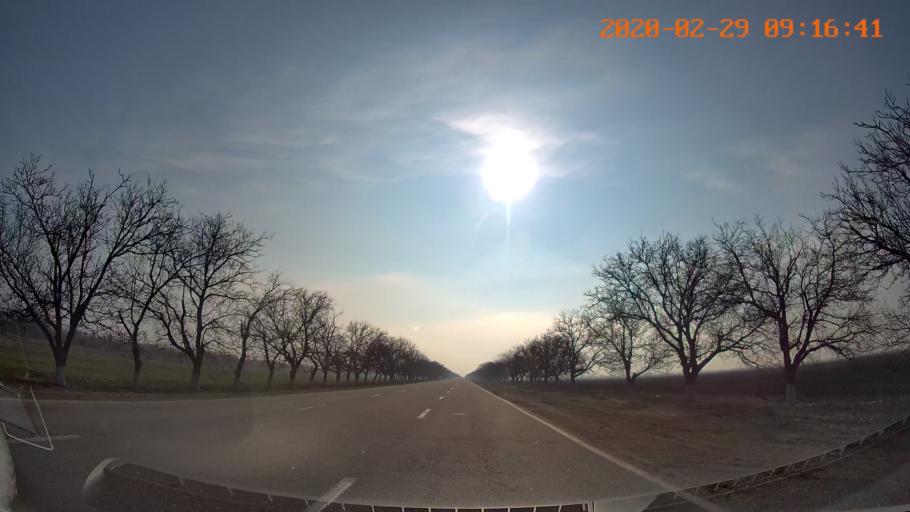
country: MD
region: Telenesti
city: Pervomaisc
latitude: 46.7896
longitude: 29.8910
